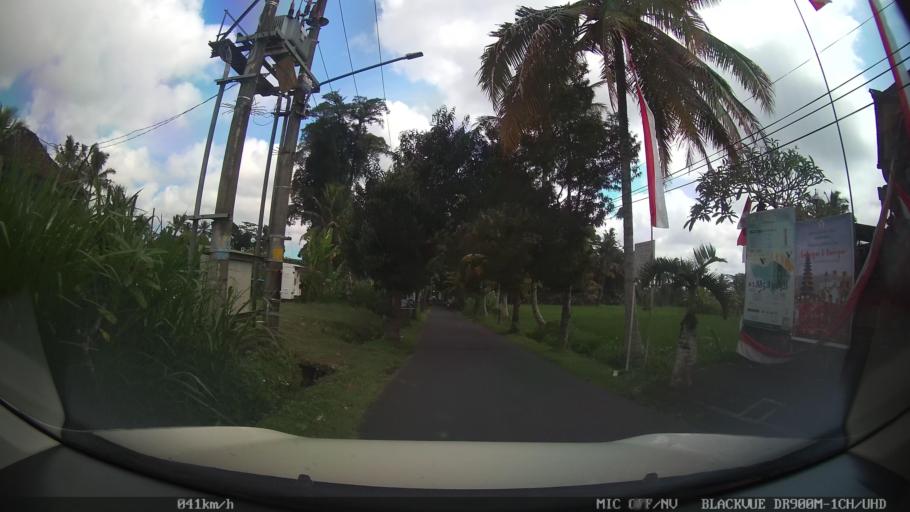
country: ID
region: Bali
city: Banjar Madangan Kaja
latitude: -8.4772
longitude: 115.3235
